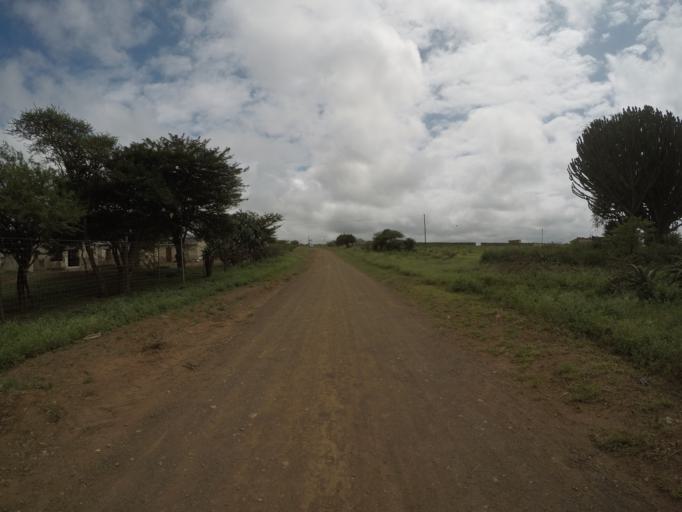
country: ZA
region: KwaZulu-Natal
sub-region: uThungulu District Municipality
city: Empangeni
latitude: -28.5803
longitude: 31.8495
